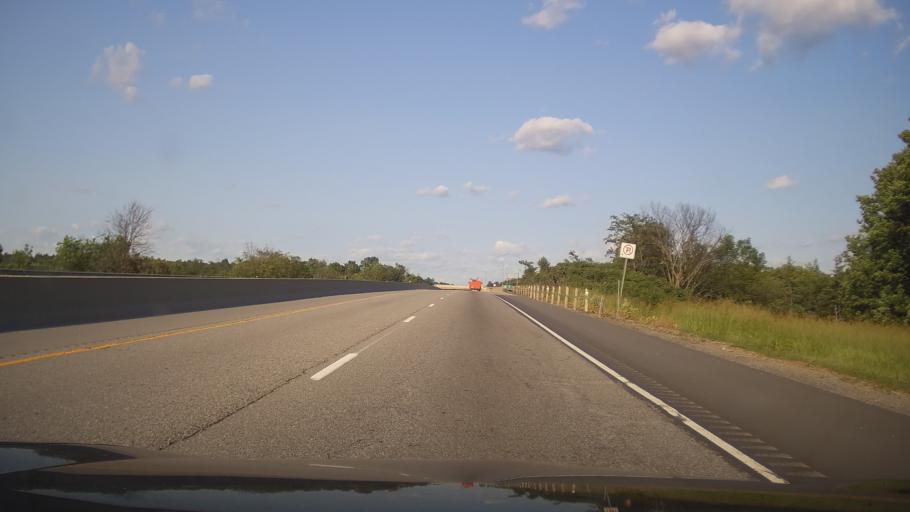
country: CA
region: Ontario
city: Gananoque
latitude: 44.3430
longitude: -76.1788
